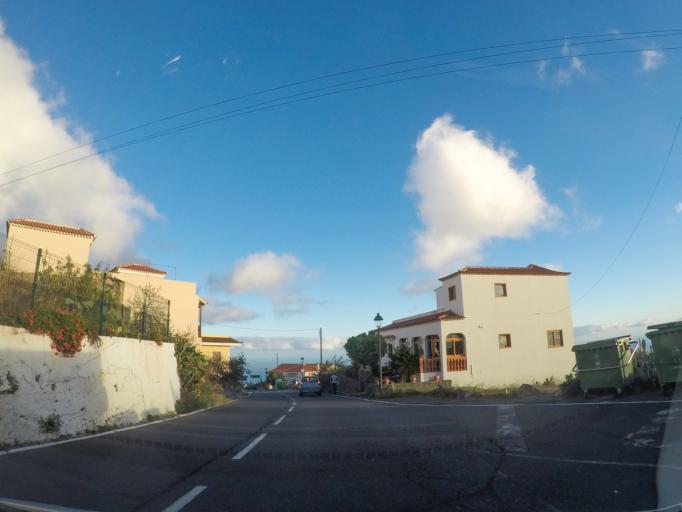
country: ES
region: Canary Islands
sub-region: Provincia de Santa Cruz de Tenerife
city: Alajero
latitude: 28.0576
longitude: -17.2342
